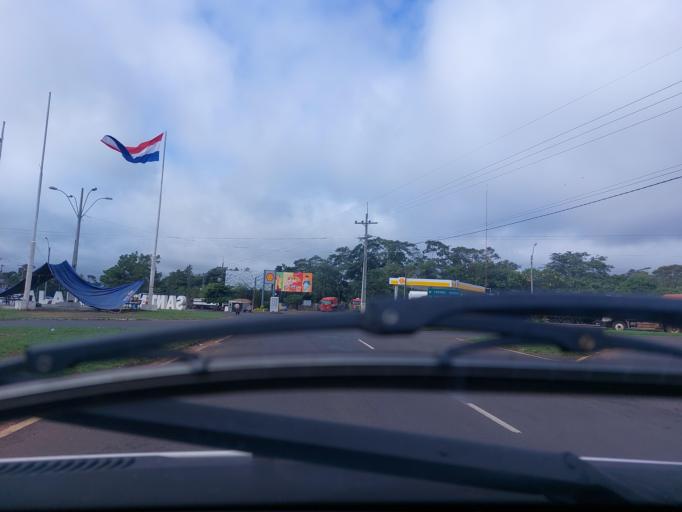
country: PY
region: San Pedro
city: Guayaybi
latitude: -24.5850
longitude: -56.4014
